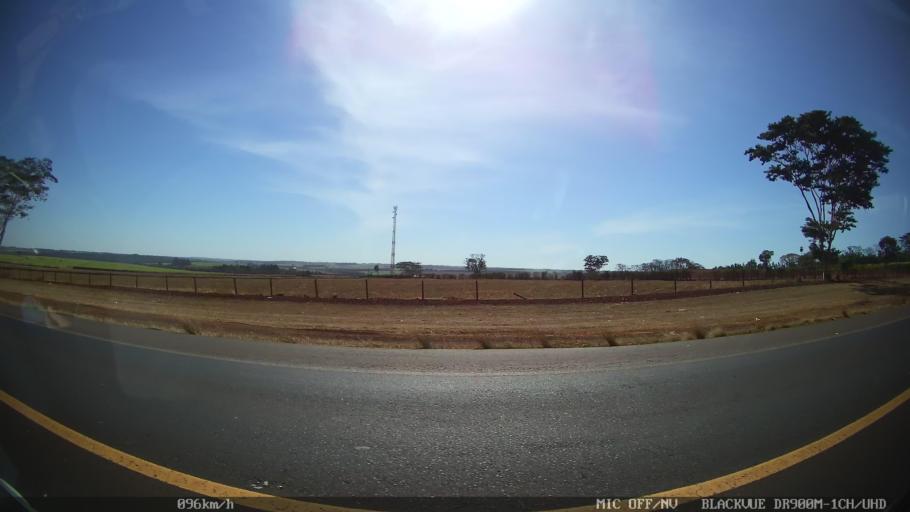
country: BR
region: Sao Paulo
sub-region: Barretos
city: Barretos
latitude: -20.5768
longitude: -48.6823
